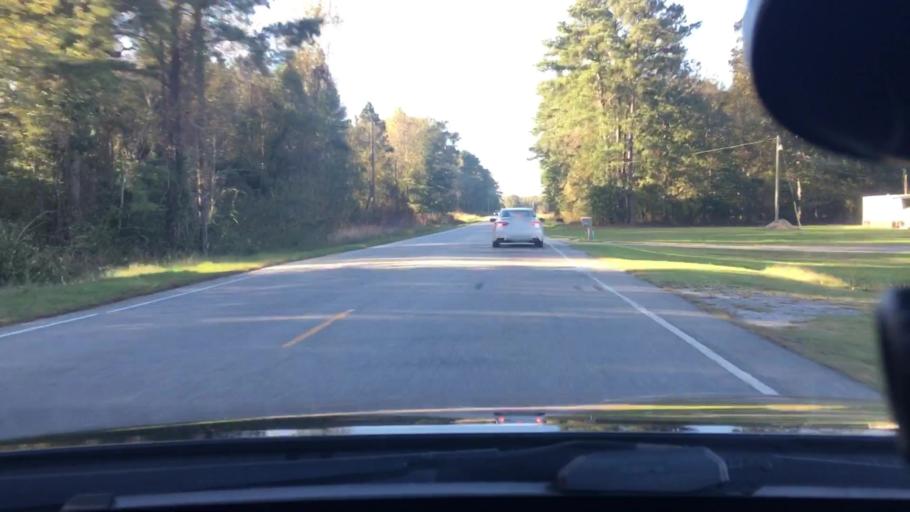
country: US
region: North Carolina
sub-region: Pitt County
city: Windsor
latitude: 35.4788
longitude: -77.2976
